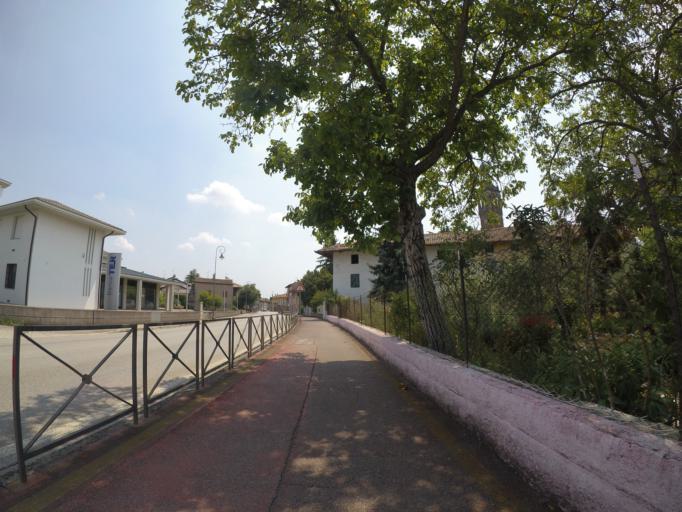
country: IT
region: Friuli Venezia Giulia
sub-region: Provincia di Udine
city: Basiliano-Vissandone
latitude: 46.0172
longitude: 13.1071
